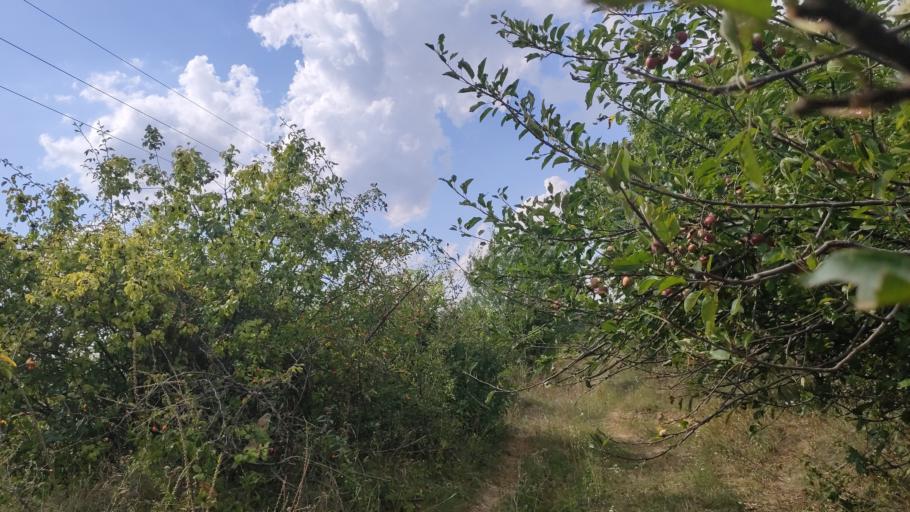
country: HU
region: Pest
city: Toeroekbalint
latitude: 47.4530
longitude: 18.8699
